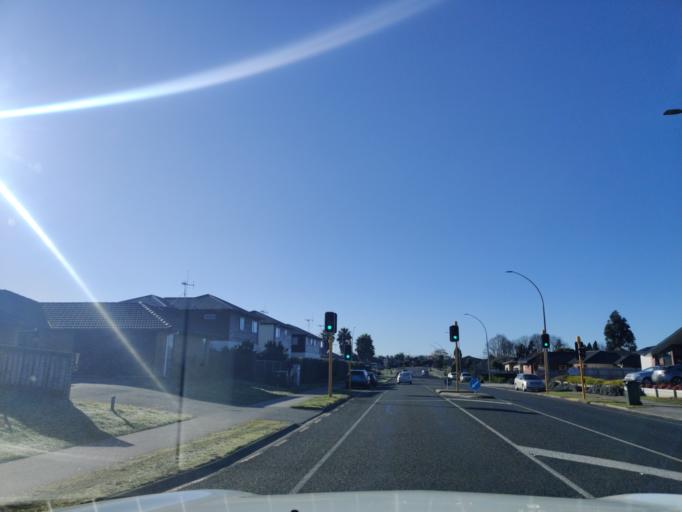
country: NZ
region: Waikato
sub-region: Hamilton City
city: Hamilton
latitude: -37.7308
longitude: 175.2767
